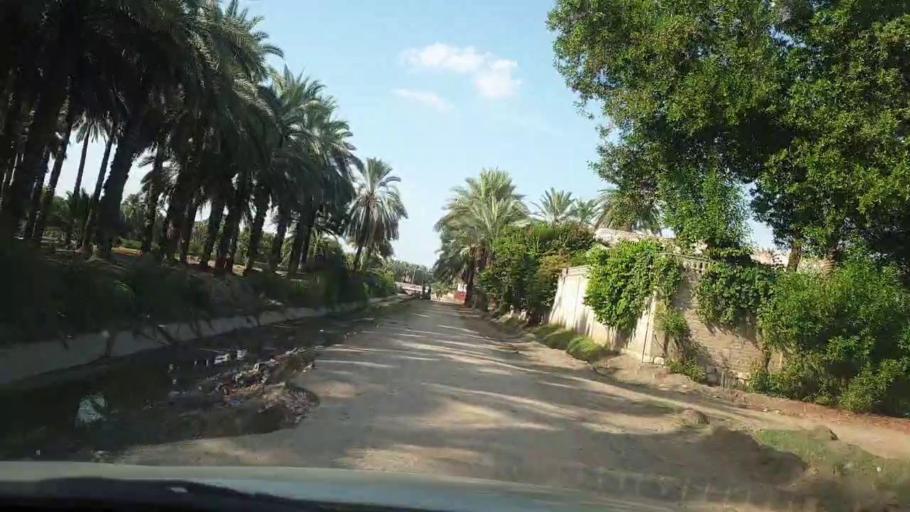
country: PK
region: Sindh
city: Sukkur
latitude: 27.6588
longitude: 68.8326
